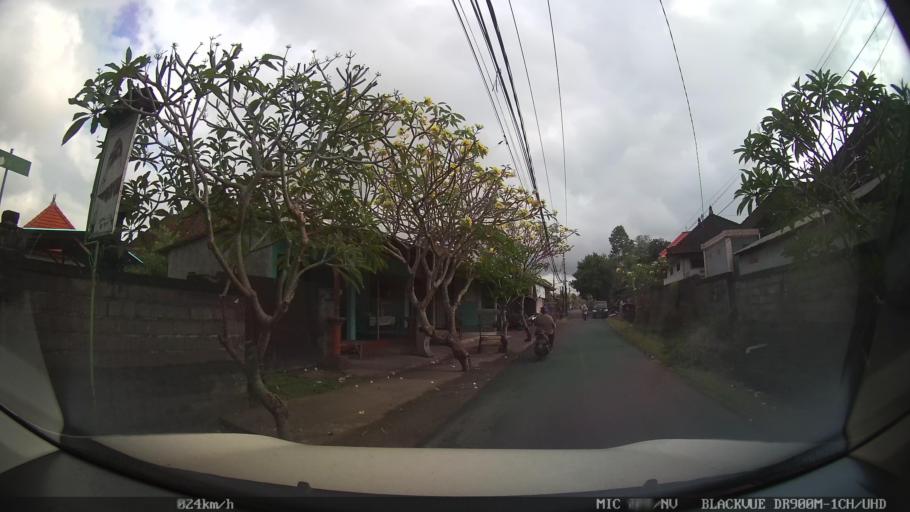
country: ID
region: Bali
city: Banjar Bucu
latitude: -8.5901
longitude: 115.2055
